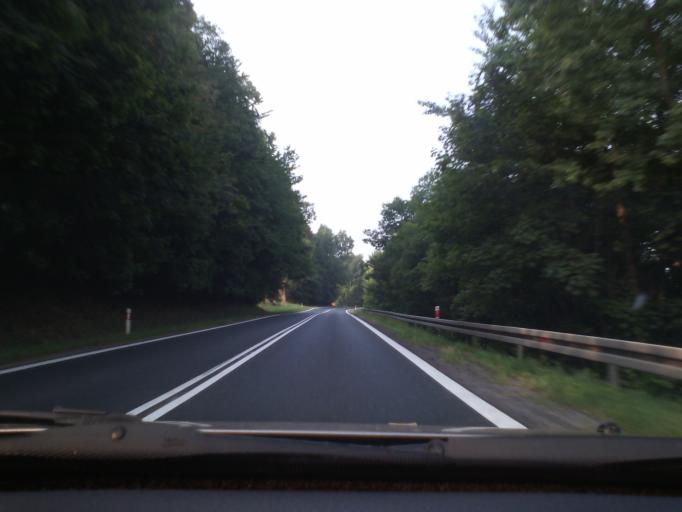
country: PL
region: Lower Silesian Voivodeship
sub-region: Powiat zlotoryjski
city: Wojcieszow
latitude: 50.9230
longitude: 15.9719
